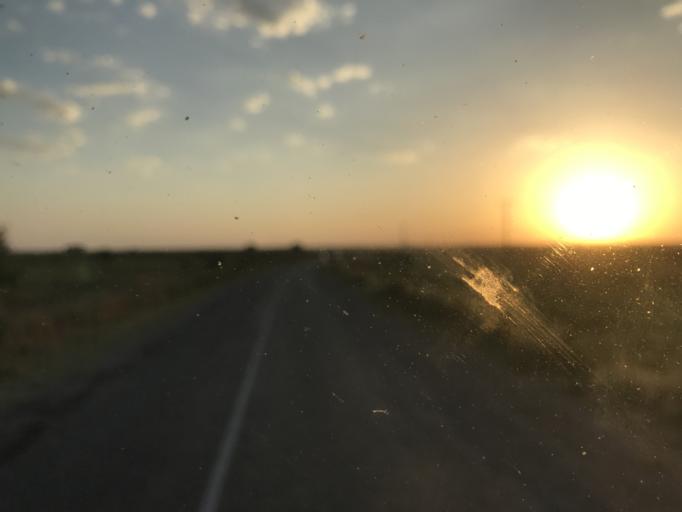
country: UZ
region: Toshkent
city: Yangiyul
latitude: 41.3800
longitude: 68.7841
